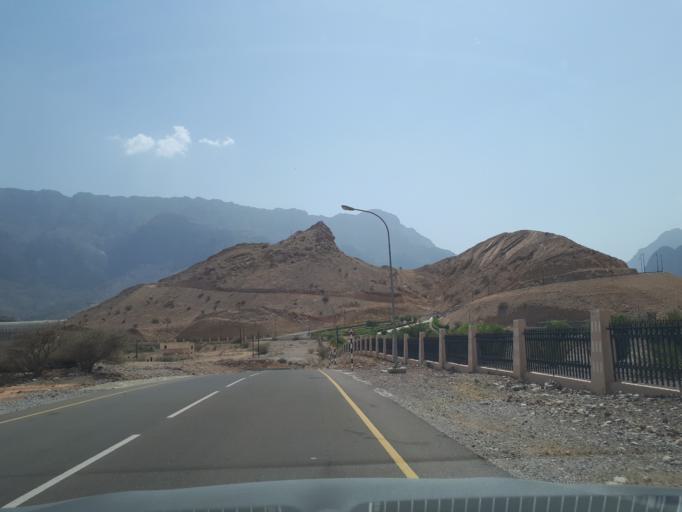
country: OM
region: Ash Sharqiyah
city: Ibra'
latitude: 23.0904
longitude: 58.8529
